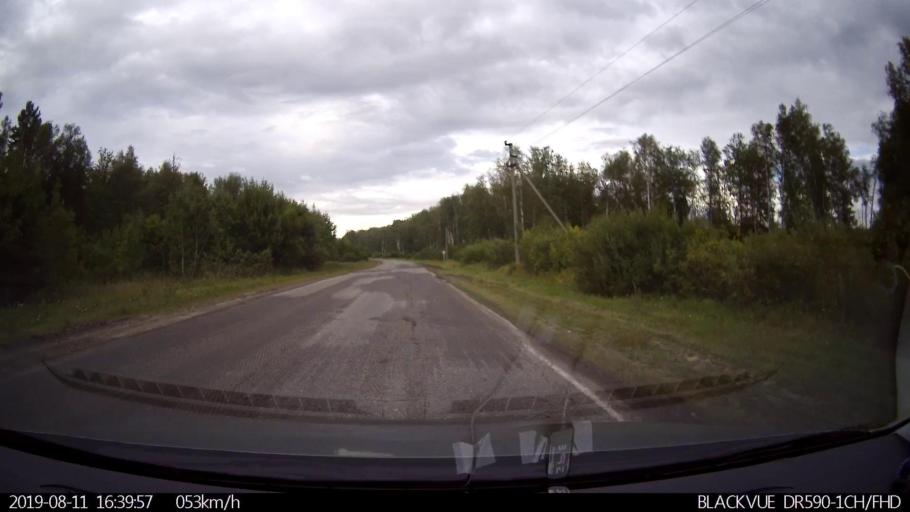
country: RU
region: Ulyanovsk
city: Mayna
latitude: 54.1428
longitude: 47.6415
